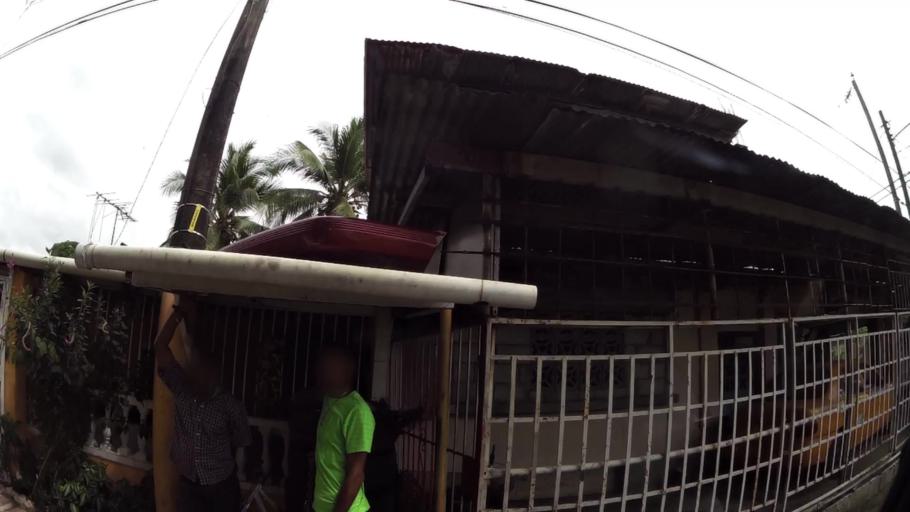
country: PA
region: Panama
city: San Miguelito
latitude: 9.0472
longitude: -79.4260
